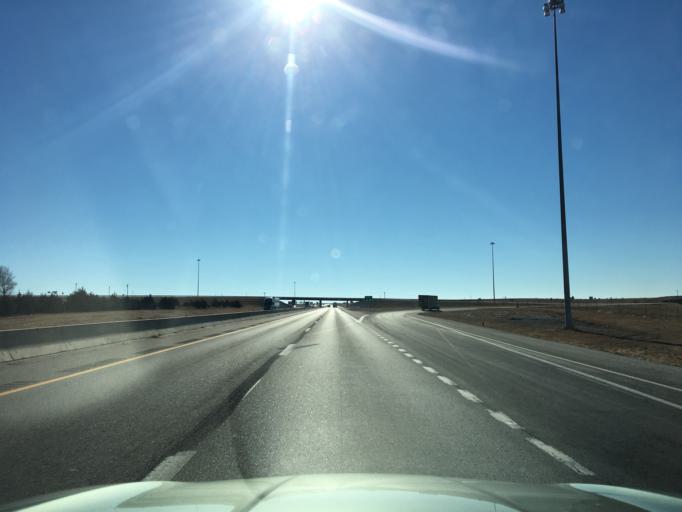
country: US
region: Kansas
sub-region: Sumner County
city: Wellington
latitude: 37.0610
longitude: -97.3385
